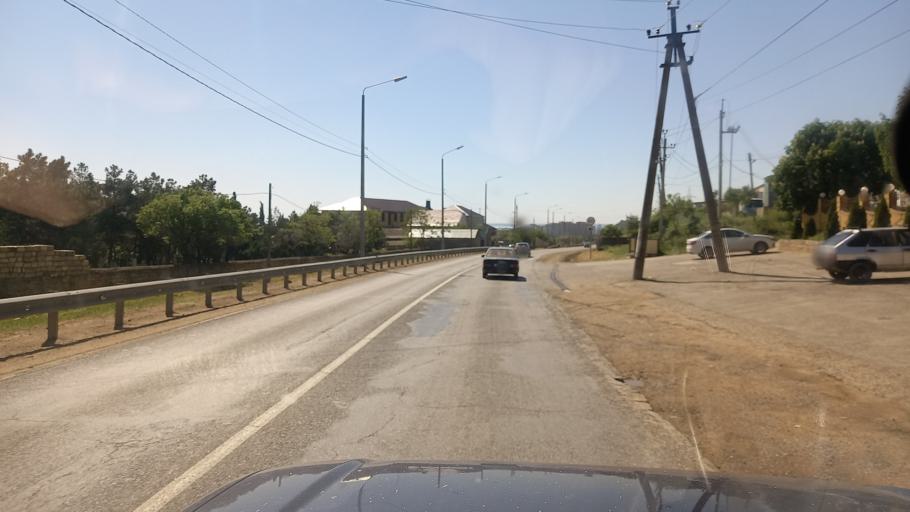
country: RU
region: Dagestan
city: Derbent
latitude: 42.0460
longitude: 48.2859
